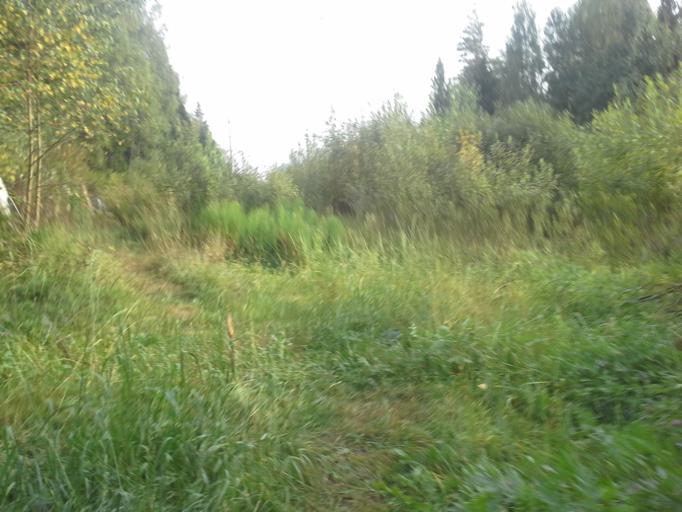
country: RU
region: Moskovskaya
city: Aprelevka
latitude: 55.5666
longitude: 37.0745
